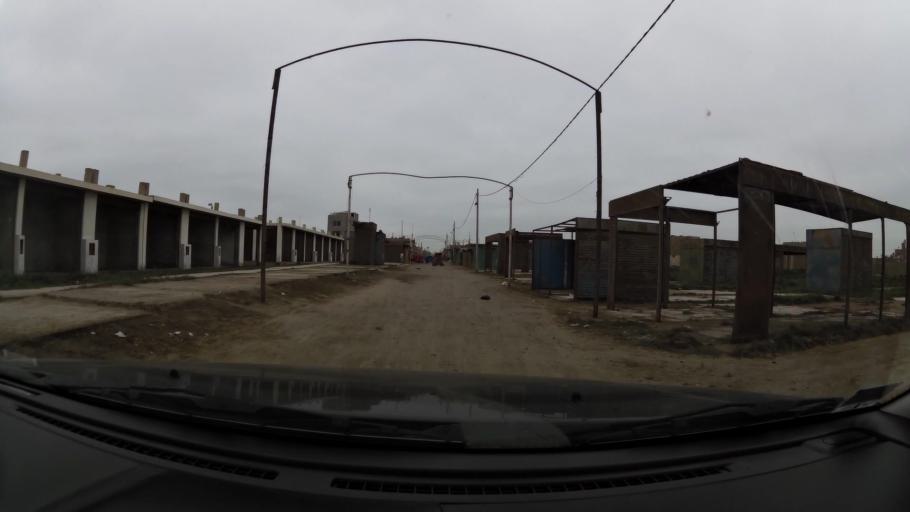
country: PE
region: Ica
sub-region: Provincia de Pisco
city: Pisco
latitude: -13.7144
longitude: -76.2112
